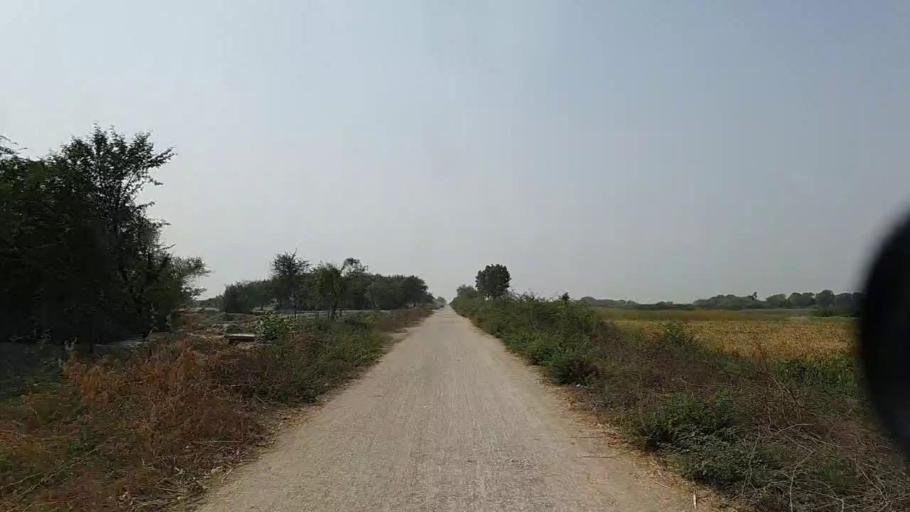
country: PK
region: Sindh
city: Naukot
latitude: 24.7695
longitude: 69.3451
